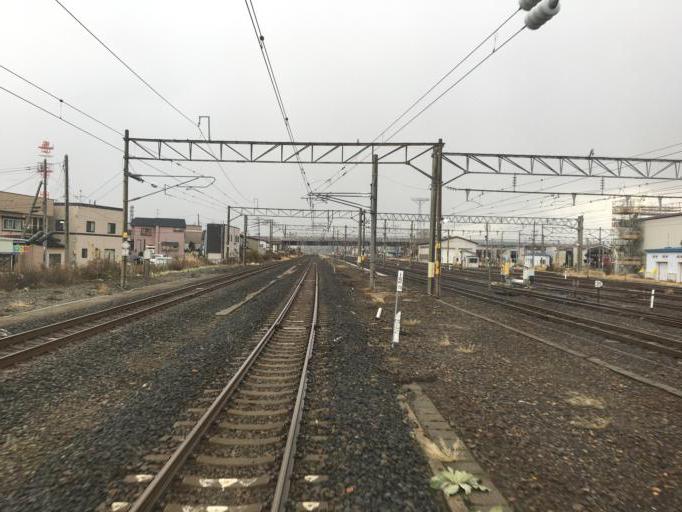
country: JP
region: Aomori
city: Aomori Shi
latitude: 40.8183
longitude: 140.7396
